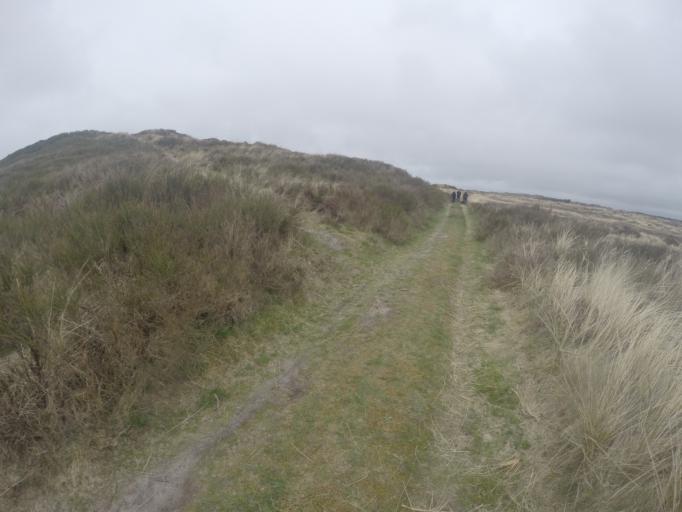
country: DK
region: North Denmark
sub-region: Thisted Kommune
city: Hurup
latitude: 56.8564
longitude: 8.2901
